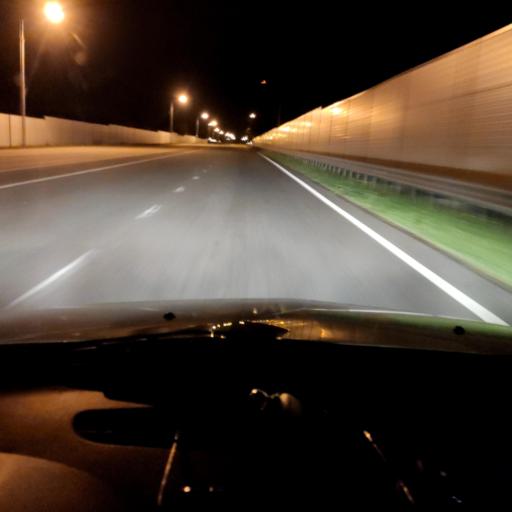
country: RU
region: Belgorod
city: Gubkin
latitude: 51.1946
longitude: 37.4505
